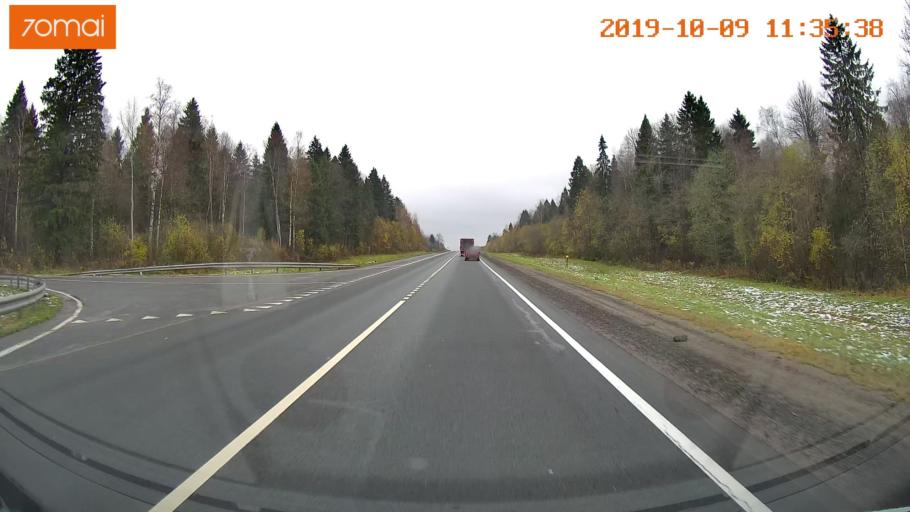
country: RU
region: Vologda
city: Gryazovets
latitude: 59.0007
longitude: 40.1282
